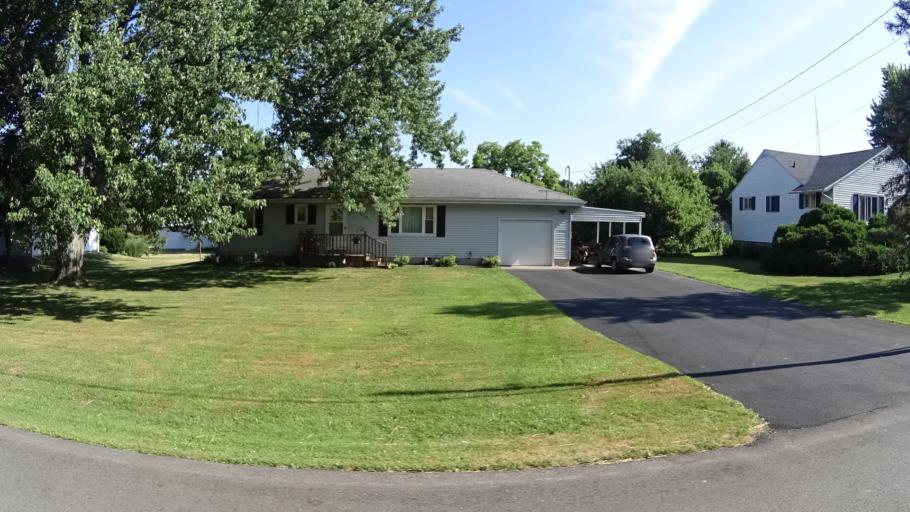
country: US
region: Ohio
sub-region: Huron County
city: Bellevue
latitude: 41.3748
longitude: -82.8182
